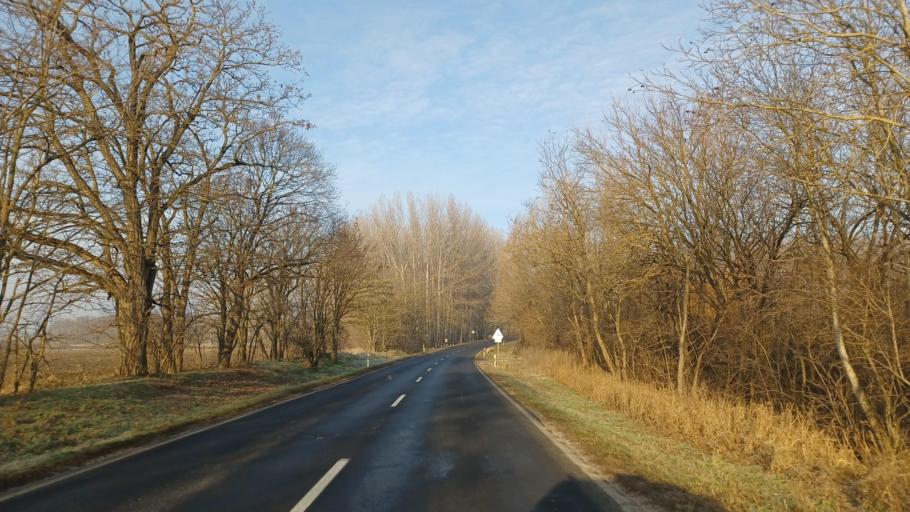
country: HU
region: Fejer
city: Cece
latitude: 46.7455
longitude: 18.6465
